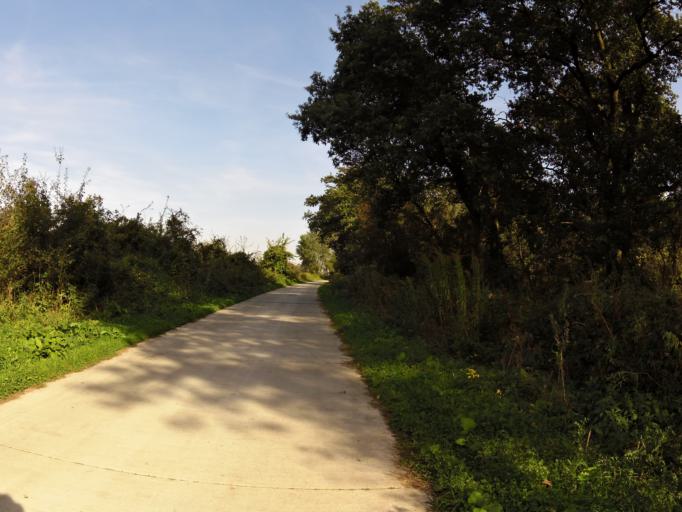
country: NL
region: Gelderland
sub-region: Gemeente Duiven
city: Duiven
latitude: 51.8797
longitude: 6.0068
